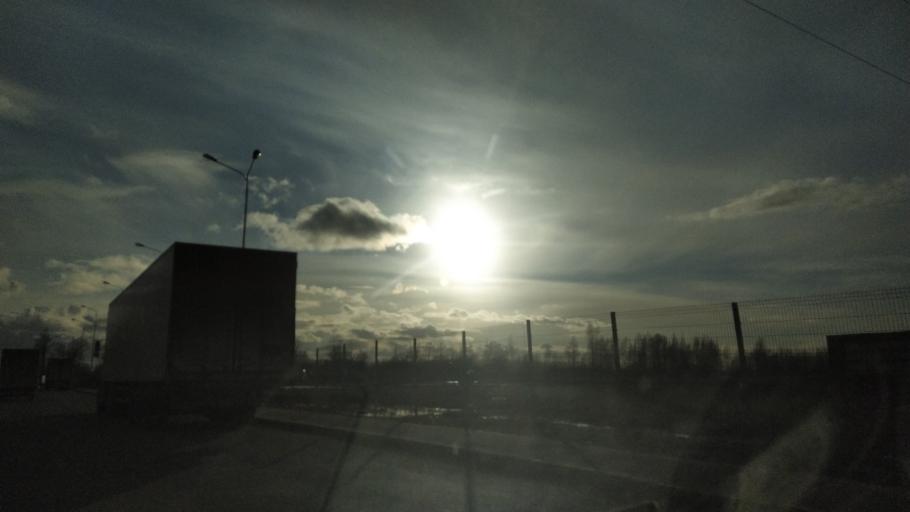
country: RU
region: St.-Petersburg
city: Petro-Slavyanka
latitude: 59.7736
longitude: 30.4563
